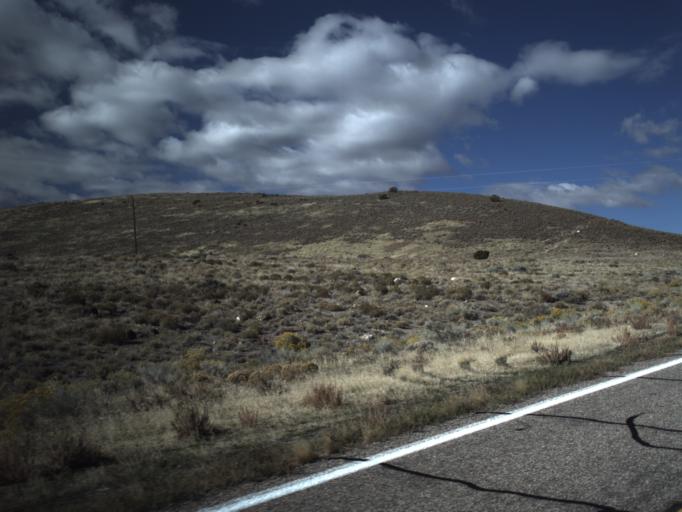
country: US
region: Utah
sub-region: Beaver County
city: Milford
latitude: 38.4572
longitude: -113.2250
